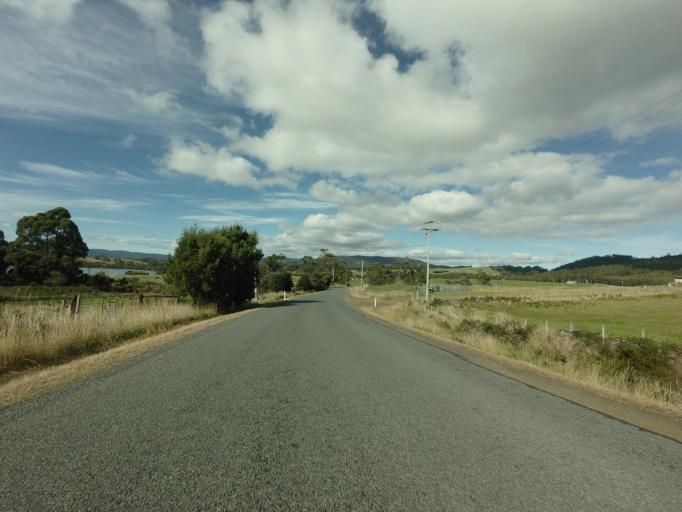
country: AU
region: Tasmania
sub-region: Clarence
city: Sandford
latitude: -43.0403
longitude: 147.7427
